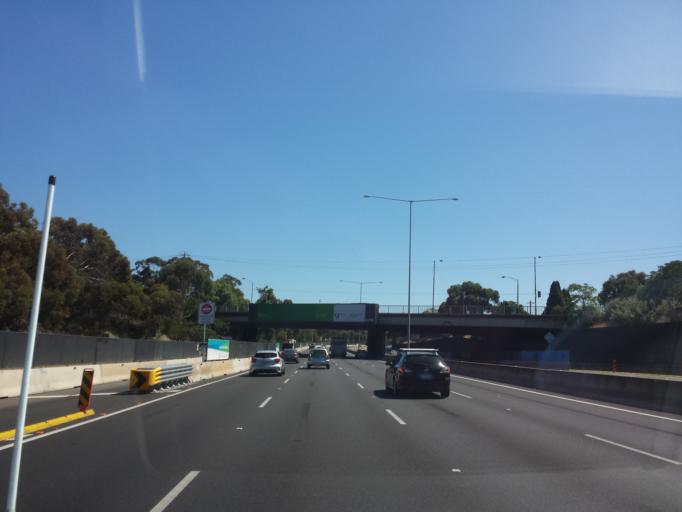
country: AU
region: Victoria
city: Brunswick West
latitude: -37.7529
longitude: 144.9360
